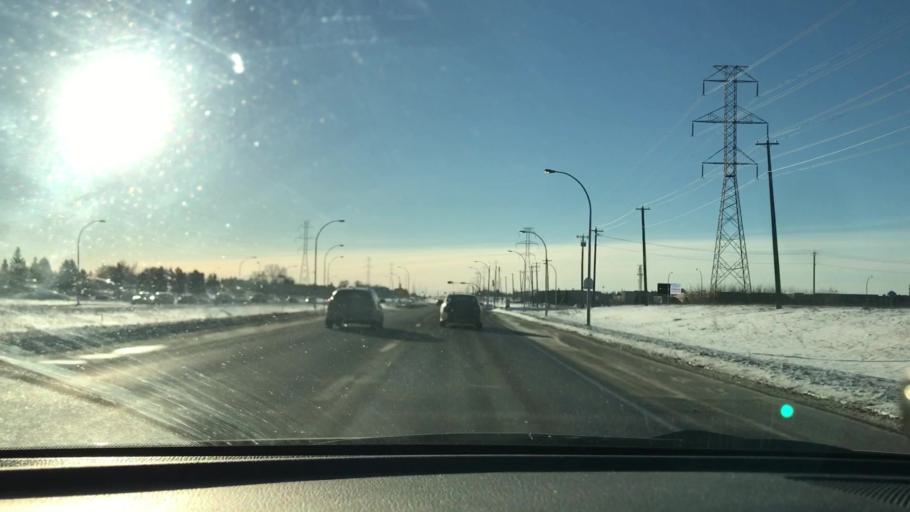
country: CA
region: Alberta
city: Edmonton
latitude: 53.4614
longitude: -113.4670
